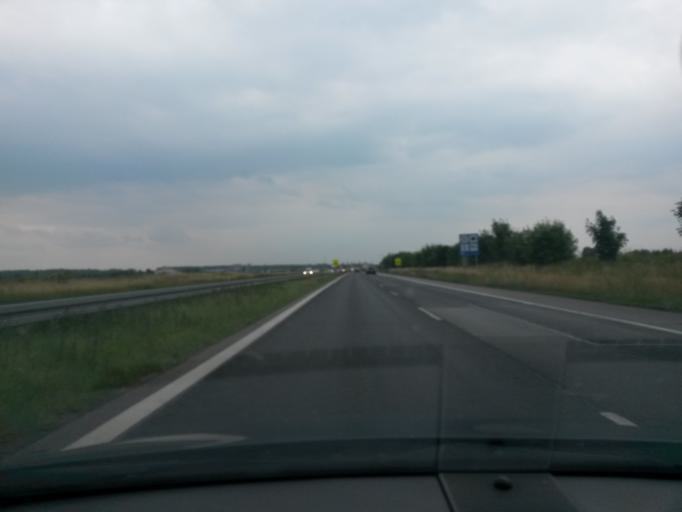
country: PL
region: Silesian Voivodeship
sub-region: Powiat czestochowski
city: Koscielec
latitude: 50.9108
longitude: 19.2106
